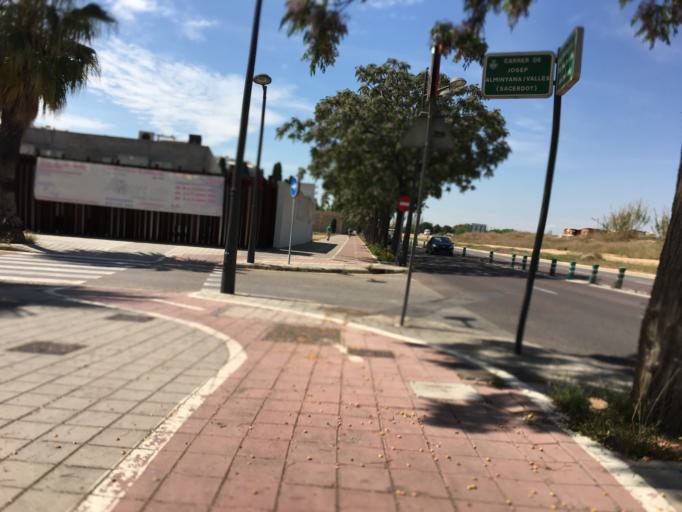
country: ES
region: Valencia
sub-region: Provincia de Valencia
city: Mislata
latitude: 39.4856
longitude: -0.4055
